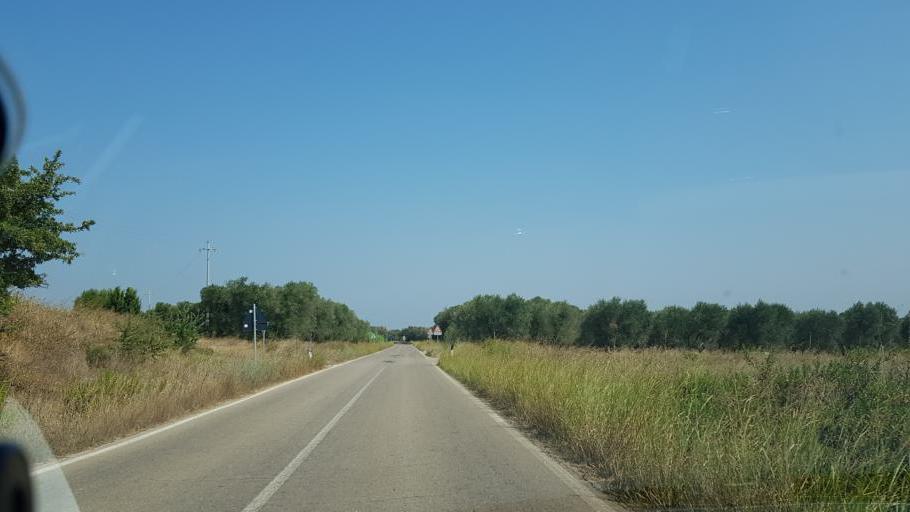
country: IT
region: Apulia
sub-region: Provincia di Brindisi
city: Torre Santa Susanna
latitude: 40.4987
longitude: 17.7337
